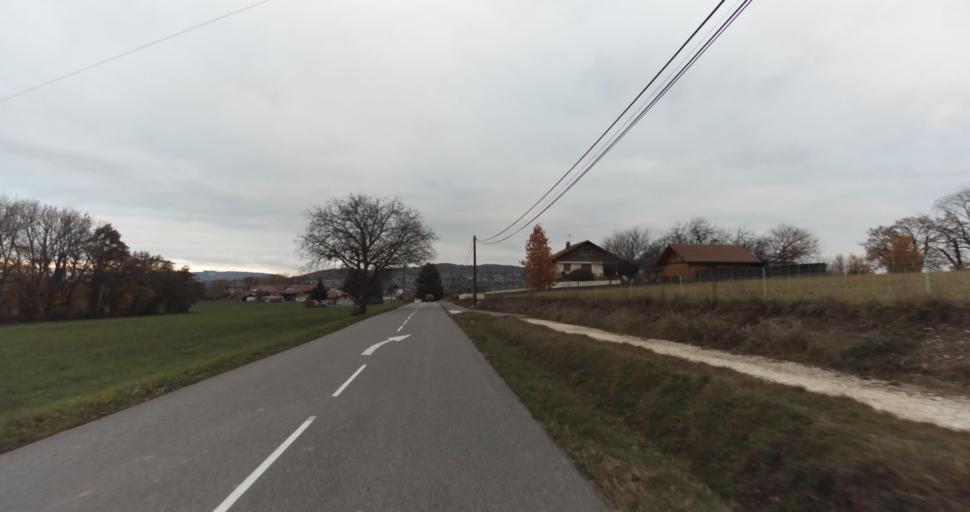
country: FR
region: Rhone-Alpes
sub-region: Departement de la Haute-Savoie
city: Chavanod
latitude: 45.8863
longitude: 6.0432
